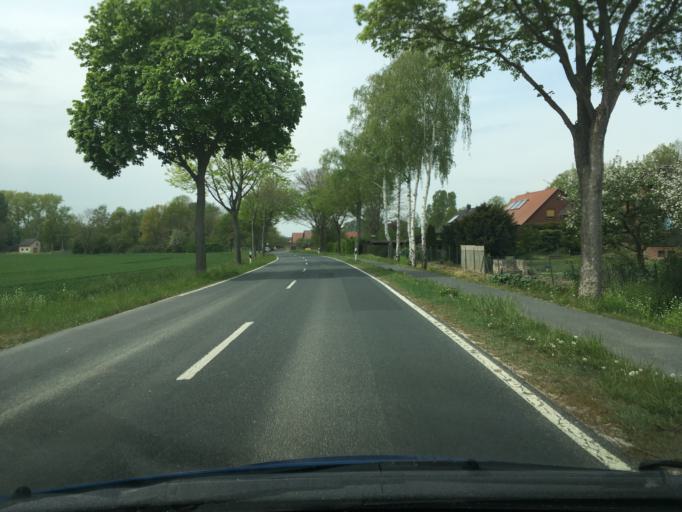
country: DE
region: Lower Saxony
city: Elze
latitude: 52.1737
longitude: 9.7230
